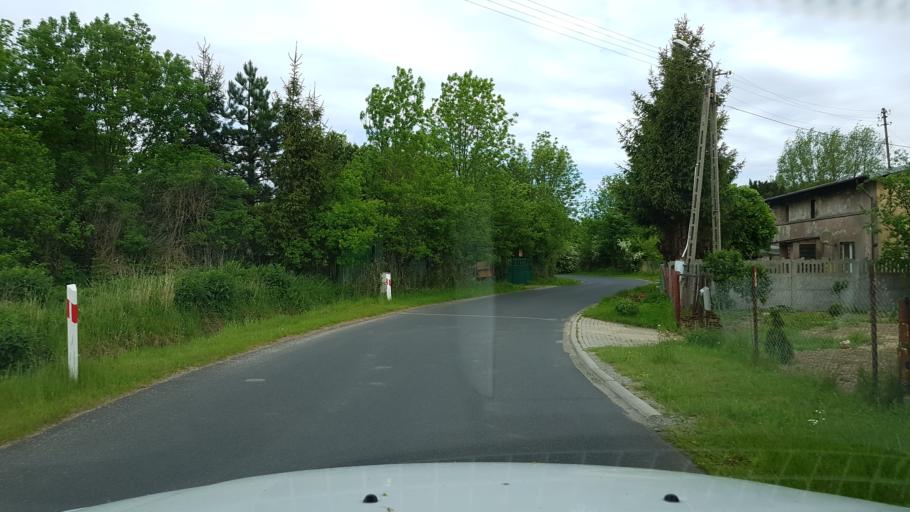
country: PL
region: West Pomeranian Voivodeship
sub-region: Powiat kolobrzeski
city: Ustronie Morskie
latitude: 54.2166
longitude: 15.8174
